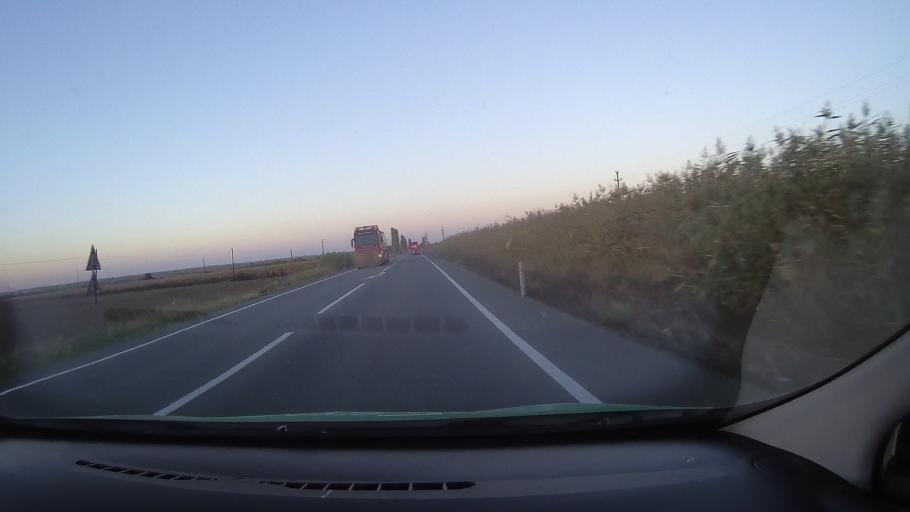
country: RO
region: Bihor
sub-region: Comuna Cherechiu
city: Cherechiu
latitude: 47.3851
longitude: 22.1443
